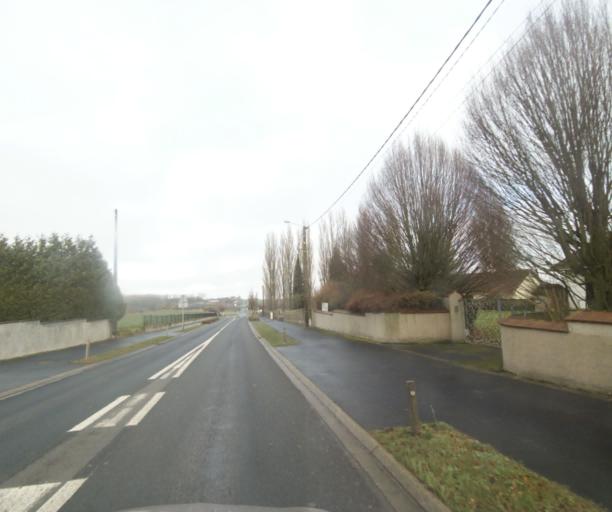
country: FR
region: Nord-Pas-de-Calais
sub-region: Departement du Nord
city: Famars
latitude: 50.2938
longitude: 3.5147
